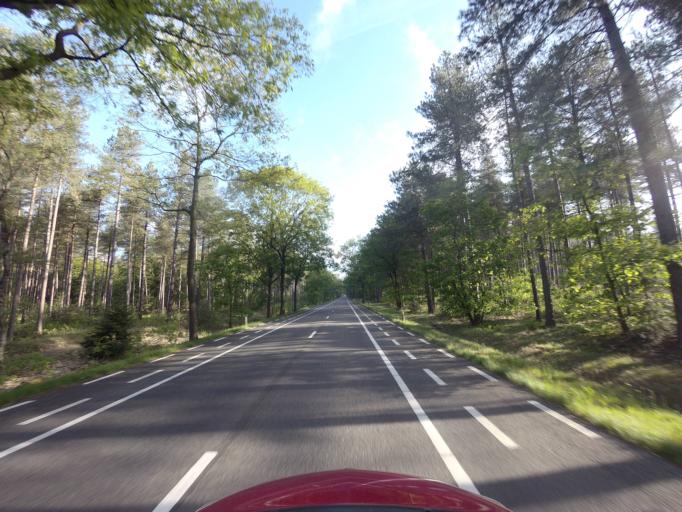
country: BE
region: Flanders
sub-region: Provincie Limburg
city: Overpelt
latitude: 51.1791
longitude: 5.3638
